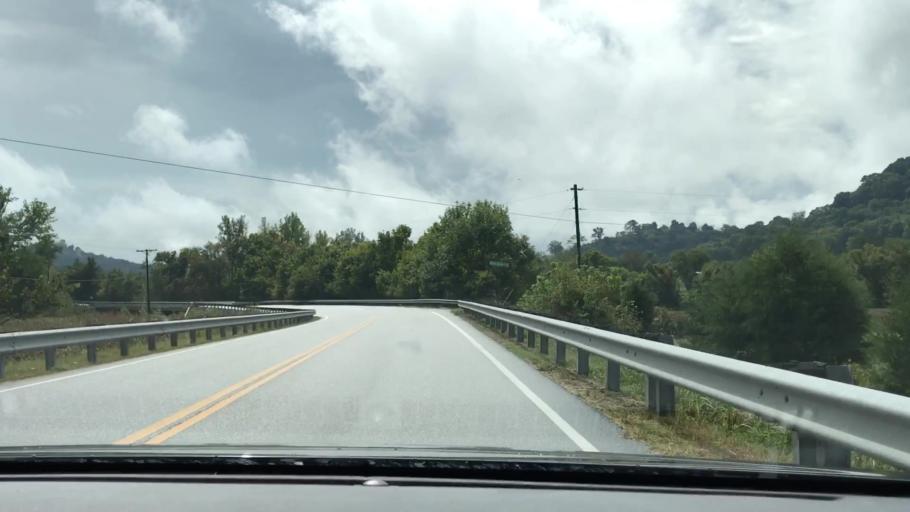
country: US
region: Tennessee
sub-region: Smith County
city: Carthage
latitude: 36.3374
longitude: -85.9657
